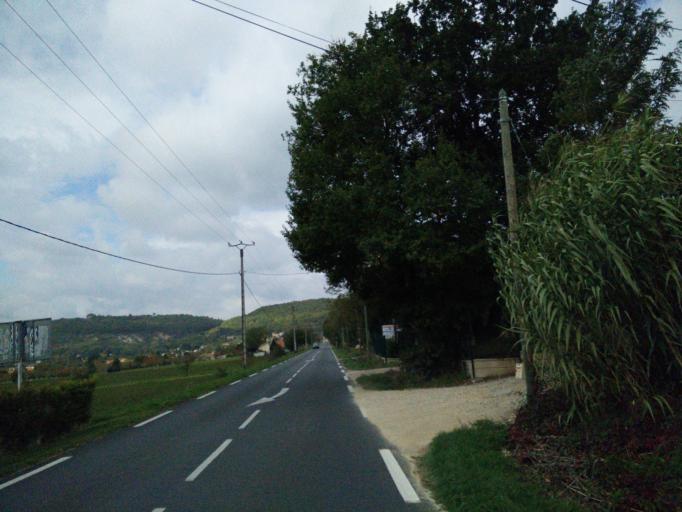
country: FR
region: Midi-Pyrenees
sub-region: Departement du Lot
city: Prayssac
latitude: 44.5056
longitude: 1.0893
